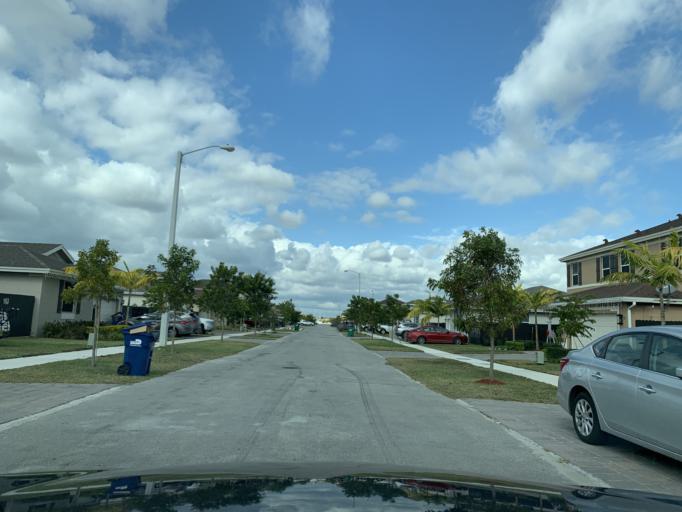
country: US
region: Florida
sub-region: Miami-Dade County
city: Naranja
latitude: 25.5082
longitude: -80.4082
